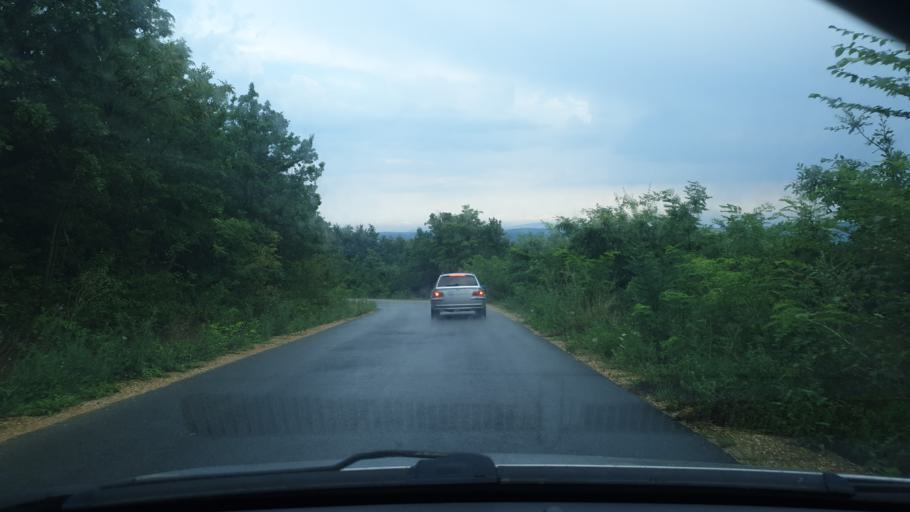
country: RS
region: Central Serbia
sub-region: Sumadijski Okrug
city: Kragujevac
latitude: 44.0529
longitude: 20.7825
